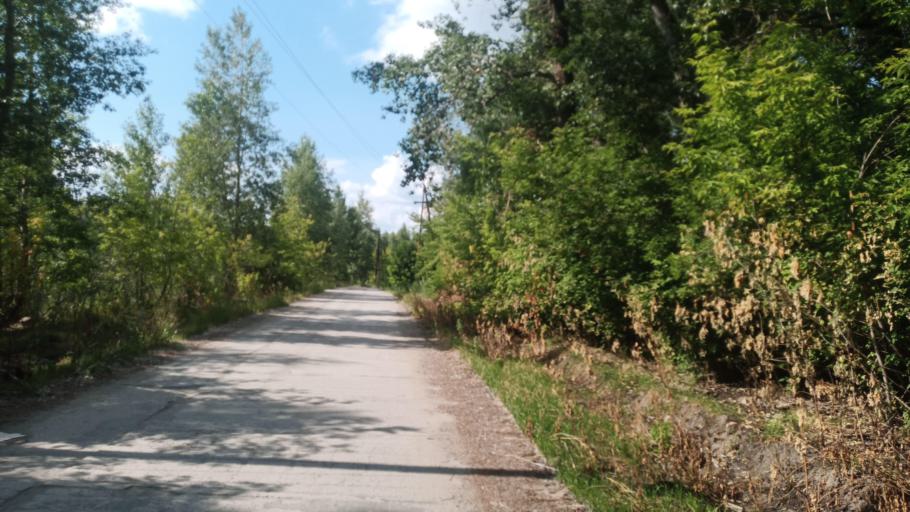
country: RU
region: Altai Krai
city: Zaton
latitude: 53.3389
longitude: 83.8063
